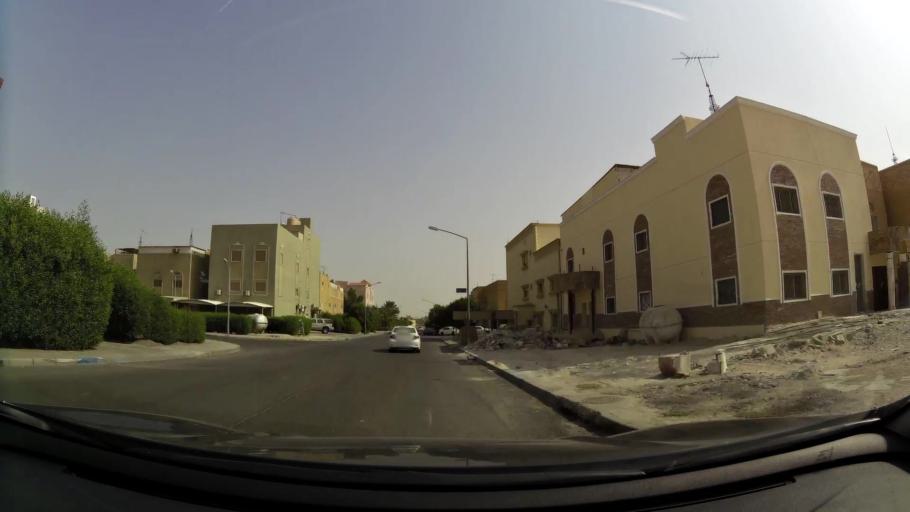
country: KW
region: Muhafazat al Jahra'
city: Al Jahra'
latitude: 29.3340
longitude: 47.6573
